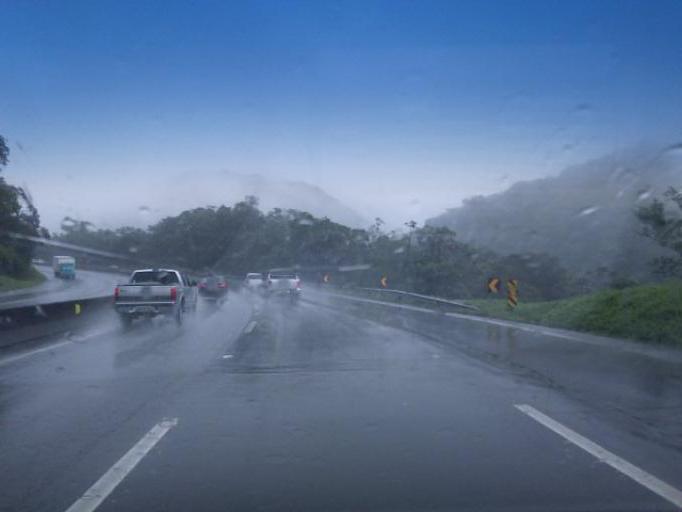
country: BR
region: Parana
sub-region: Guaratuba
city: Guaratuba
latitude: -25.8816
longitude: -48.9339
